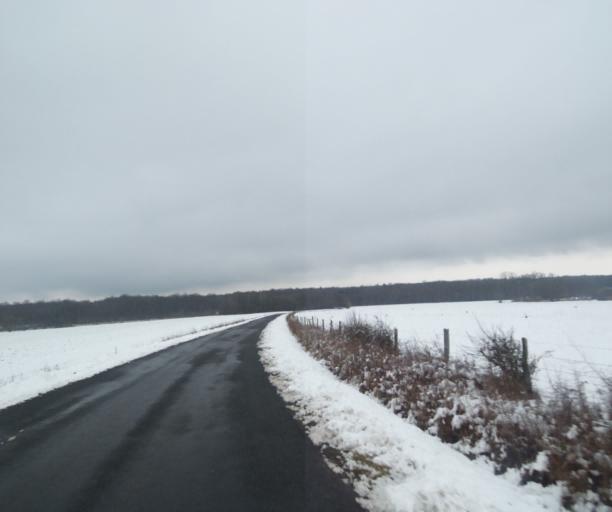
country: FR
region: Champagne-Ardenne
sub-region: Departement de la Haute-Marne
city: Laneuville-a-Remy
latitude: 48.4919
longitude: 4.8680
